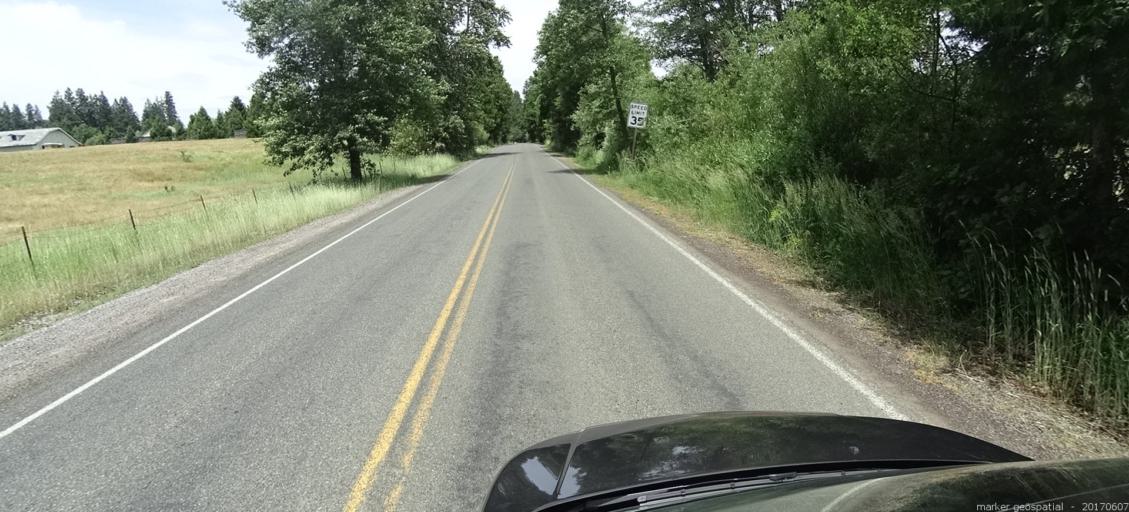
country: US
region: California
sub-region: Siskiyou County
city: Mount Shasta
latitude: 41.2983
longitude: -122.3230
